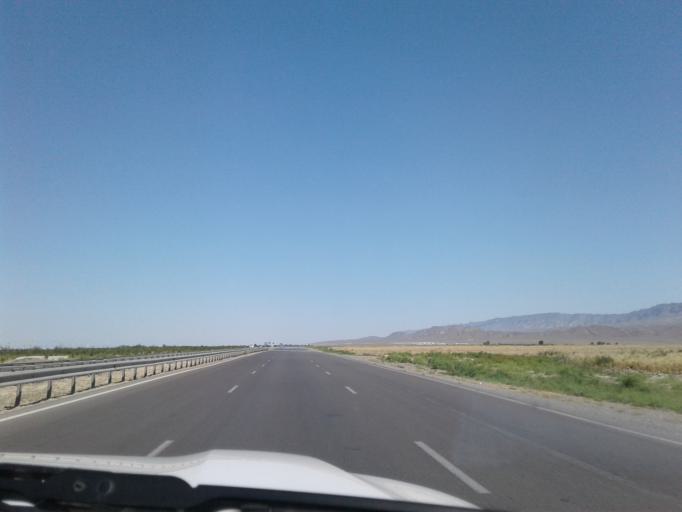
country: TM
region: Ahal
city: Annau
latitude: 37.8227
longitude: 58.7602
